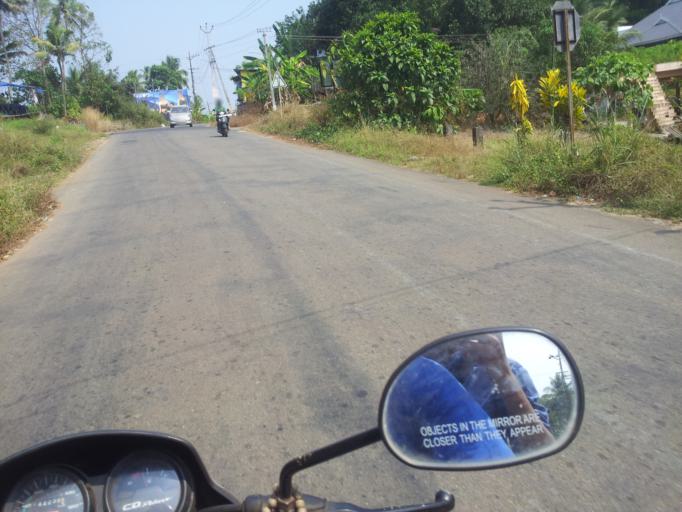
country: IN
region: Kerala
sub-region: Ernakulam
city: Muvattupuzha
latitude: 9.8952
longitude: 76.6984
